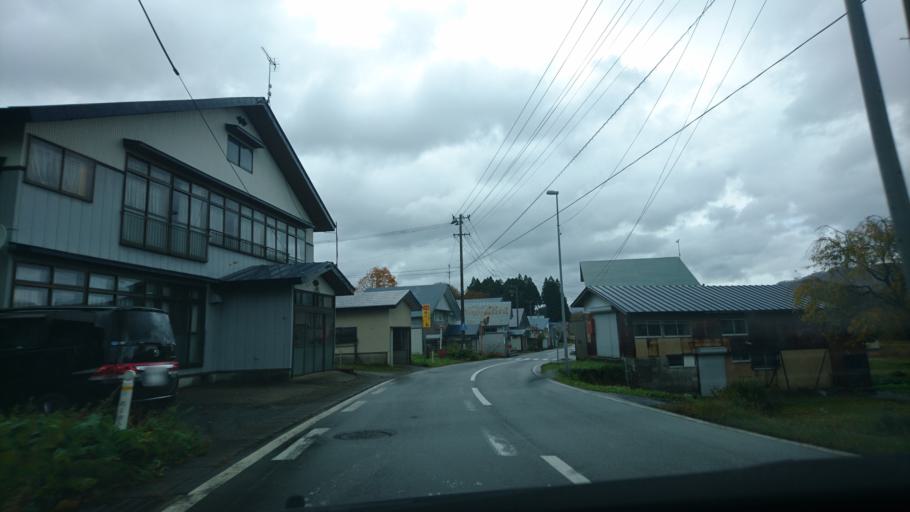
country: JP
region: Akita
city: Kakunodatemachi
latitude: 39.4589
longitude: 140.7727
